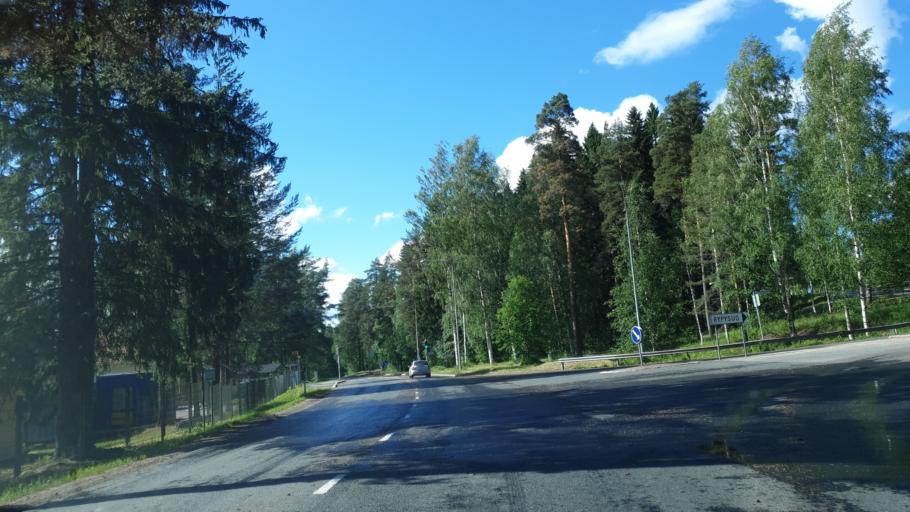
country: FI
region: Northern Savo
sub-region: Kuopio
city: Kuopio
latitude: 62.9152
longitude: 27.6352
